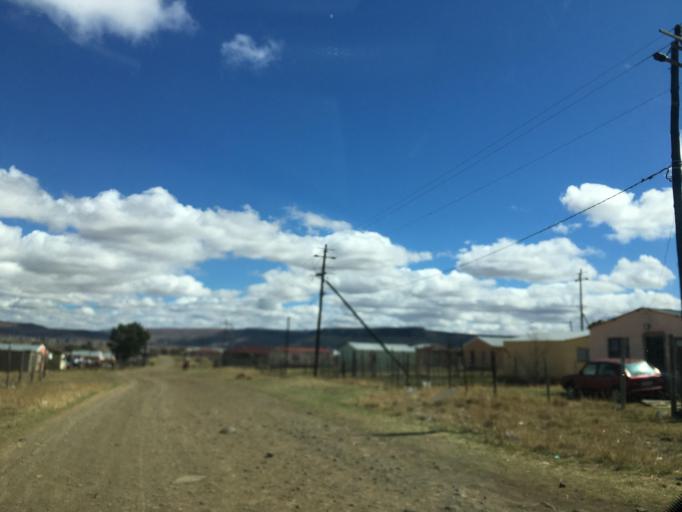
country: ZA
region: Eastern Cape
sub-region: Chris Hani District Municipality
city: Cala
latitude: -31.5424
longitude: 27.6988
